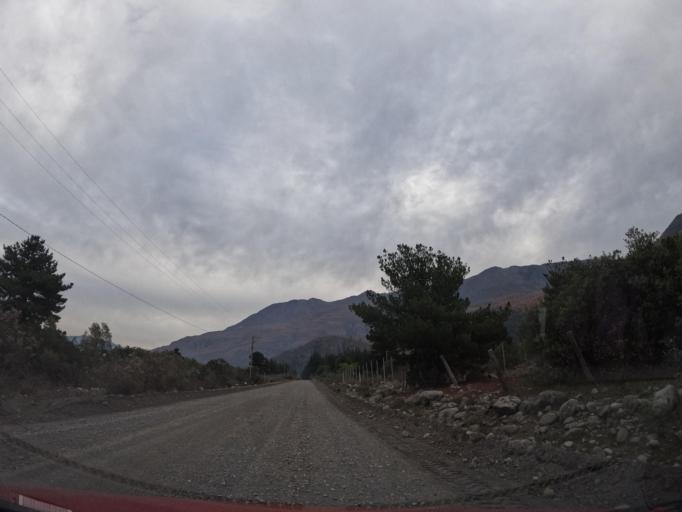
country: CL
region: Maule
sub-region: Provincia de Linares
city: Colbun
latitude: -35.7044
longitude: -71.0915
